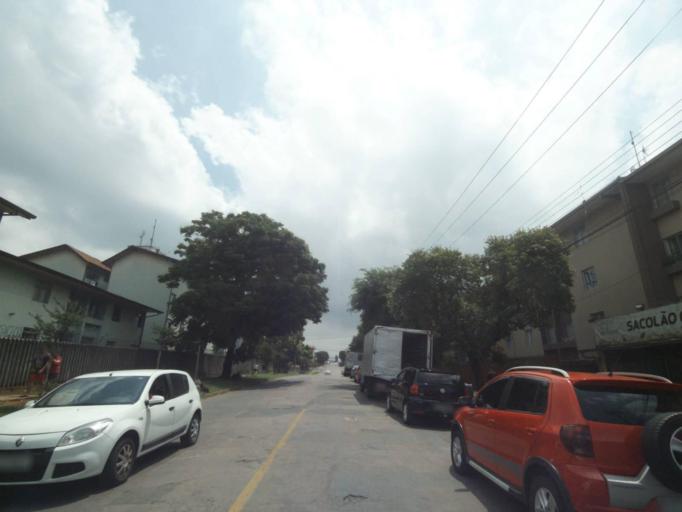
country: BR
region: Parana
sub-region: Curitiba
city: Curitiba
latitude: -25.4842
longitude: -49.3504
